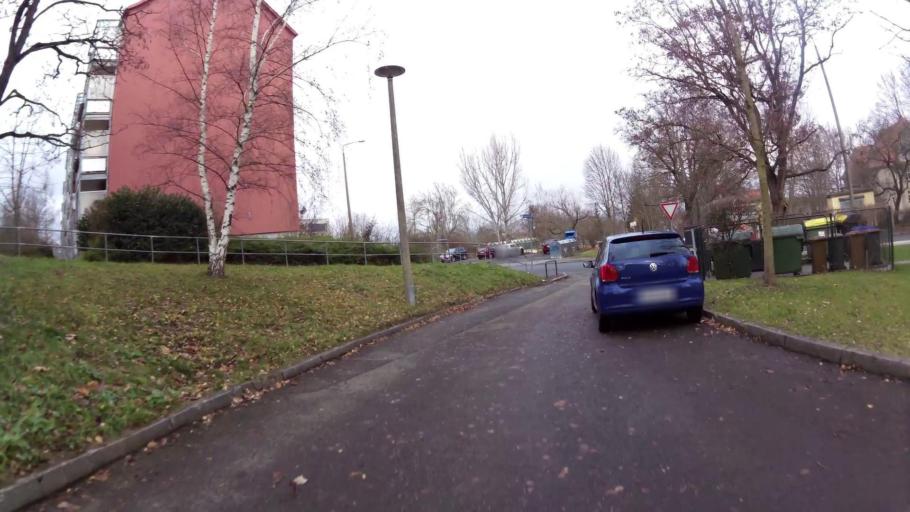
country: DE
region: Thuringia
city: Weimar
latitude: 50.9741
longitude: 11.3138
